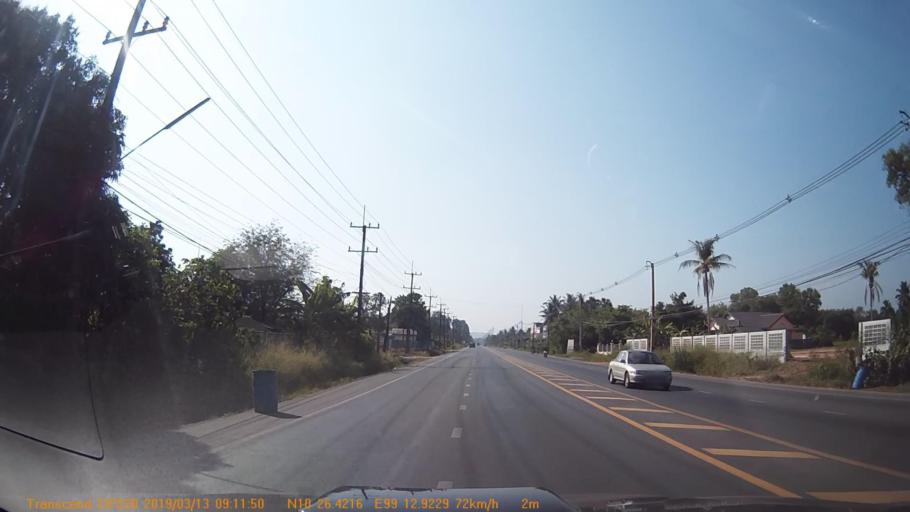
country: TH
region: Chumphon
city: Chumphon
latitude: 10.4402
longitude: 99.2155
